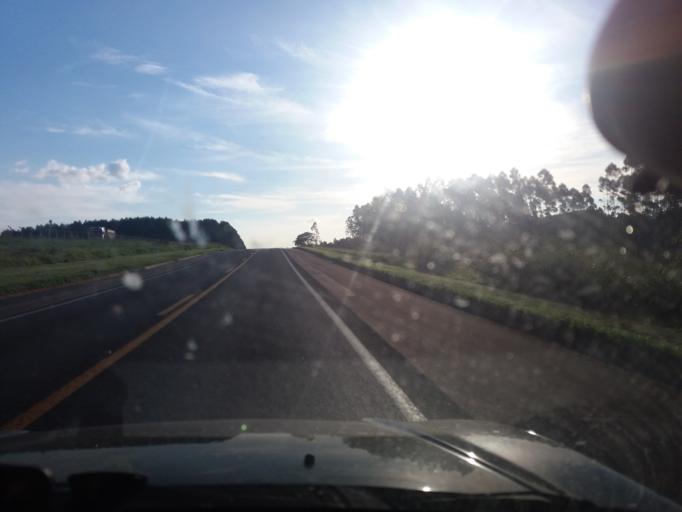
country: BR
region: Sao Paulo
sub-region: Buri
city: Buri
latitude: -23.9378
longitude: -48.6193
